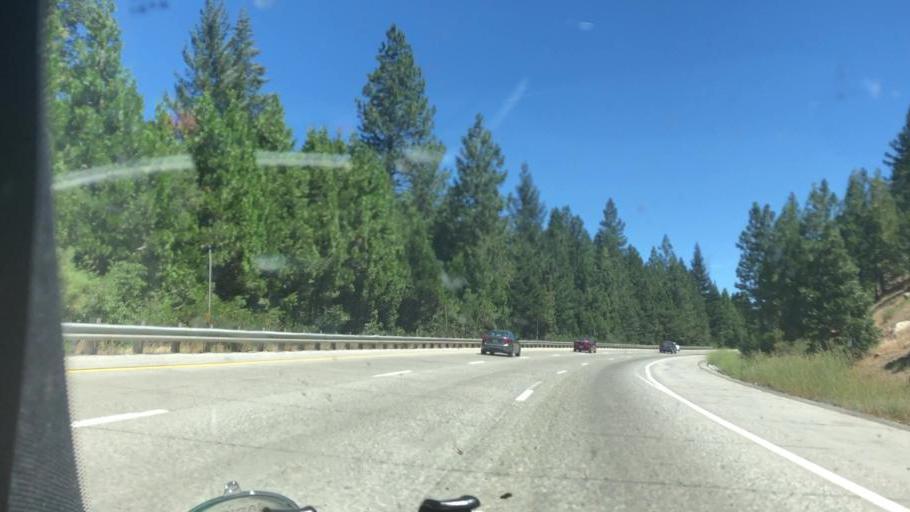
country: US
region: California
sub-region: Placer County
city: Foresthill
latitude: 39.2416
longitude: -120.7511
